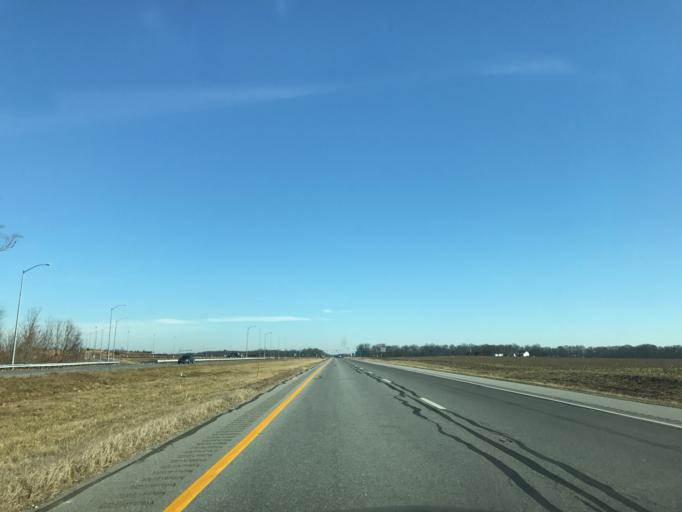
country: US
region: Delaware
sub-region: New Castle County
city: Middletown
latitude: 39.3810
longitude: -75.8038
